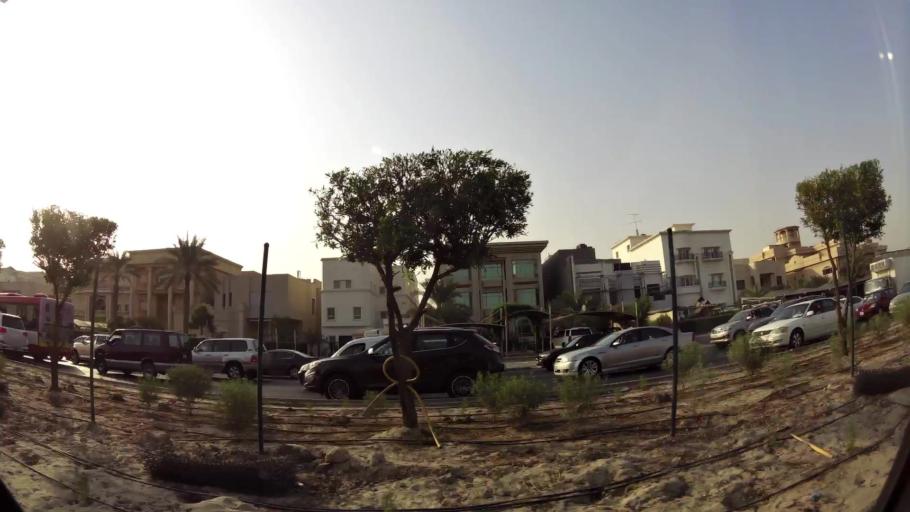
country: KW
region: Muhafazat Hawalli
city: Hawalli
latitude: 29.3215
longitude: 48.0017
